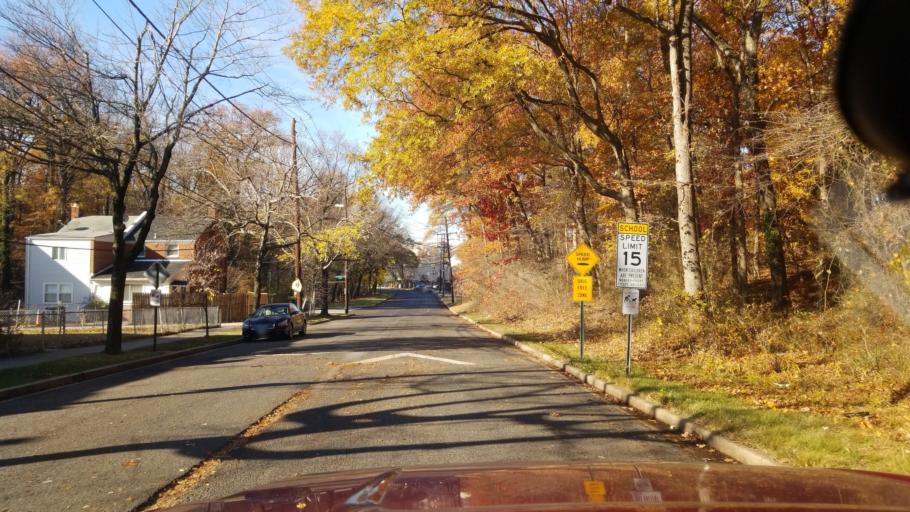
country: US
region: Maryland
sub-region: Prince George's County
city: Coral Hills
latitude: 38.8866
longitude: -76.9440
